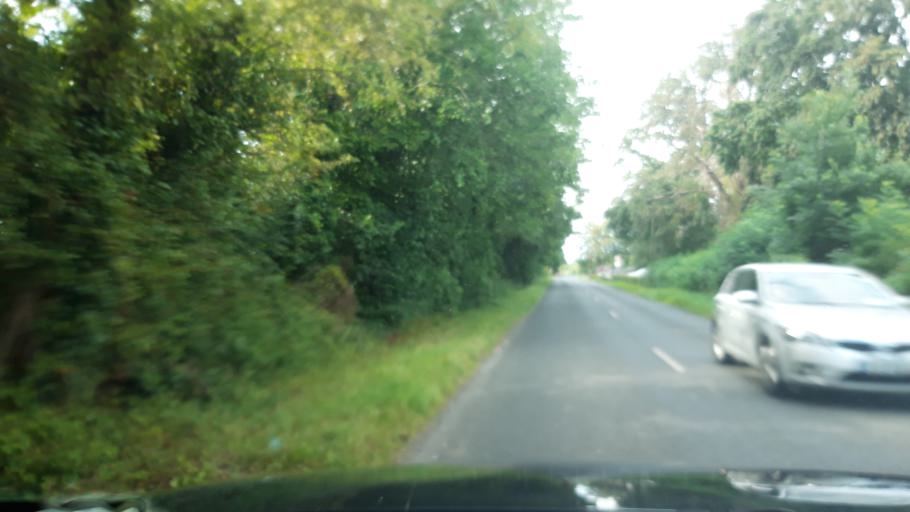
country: IE
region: Leinster
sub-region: Kildare
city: Athy
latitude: 53.0069
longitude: -6.9629
